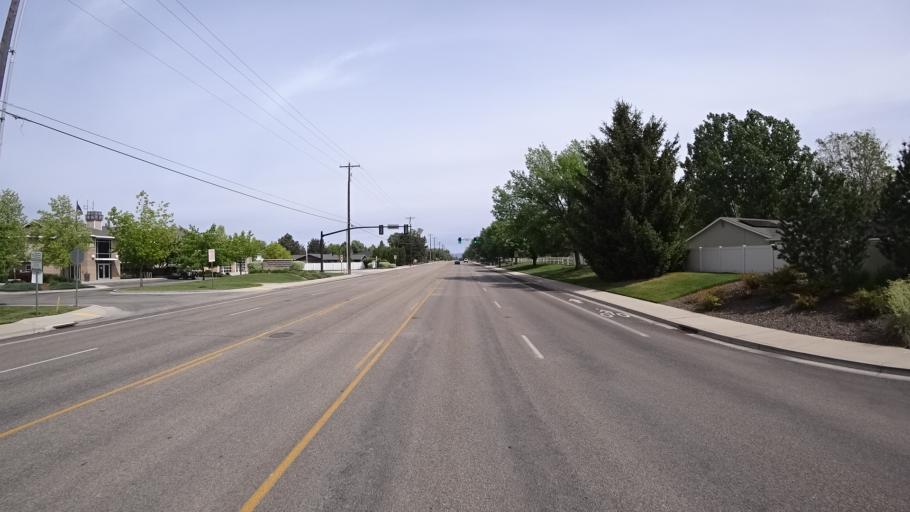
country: US
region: Idaho
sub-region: Ada County
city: Meridian
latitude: 43.5799
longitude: -116.3142
